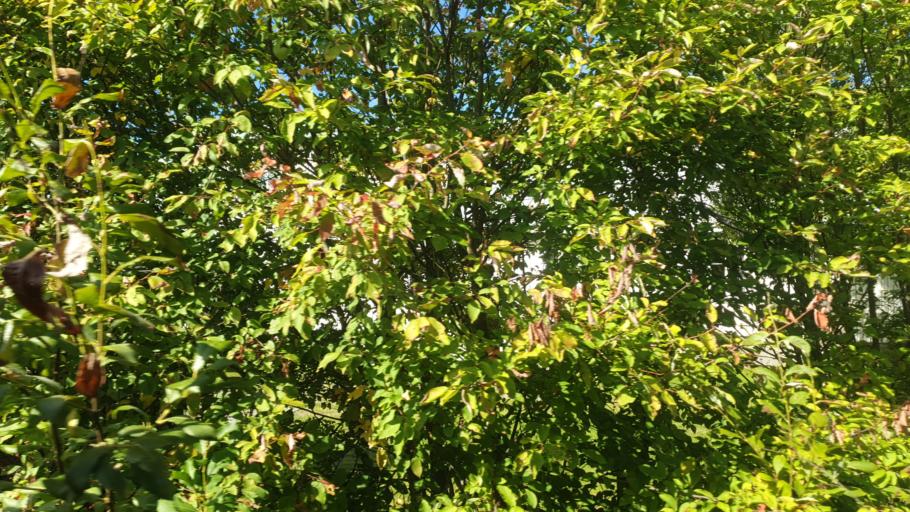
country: NO
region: Sor-Trondelag
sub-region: Orkdal
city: Orkanger
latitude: 63.2897
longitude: 9.8434
